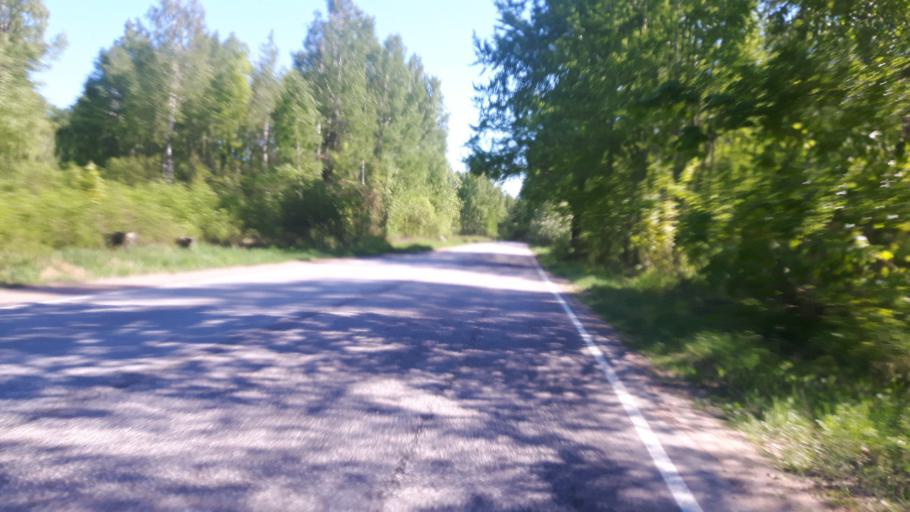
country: RU
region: Leningrad
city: Glebychevo
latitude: 60.2833
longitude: 28.8800
